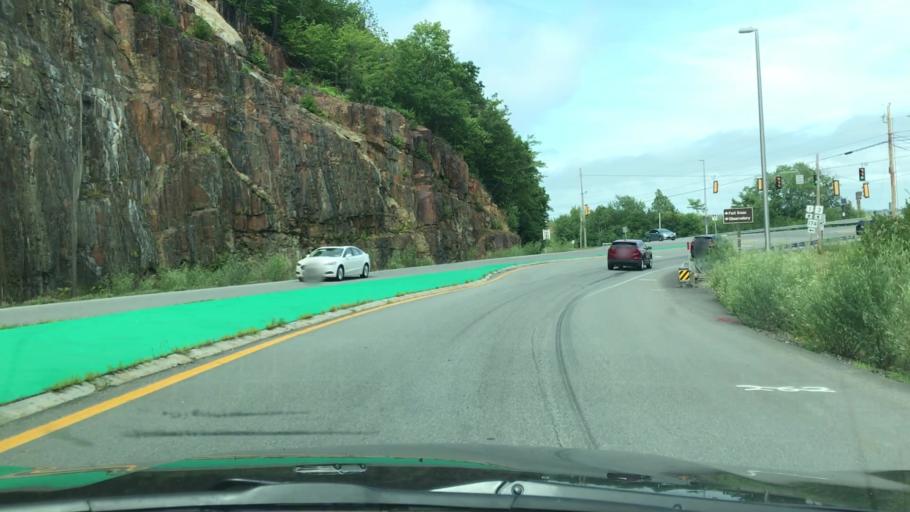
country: US
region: Maine
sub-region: Hancock County
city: Bucksport
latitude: 44.5606
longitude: -68.8069
